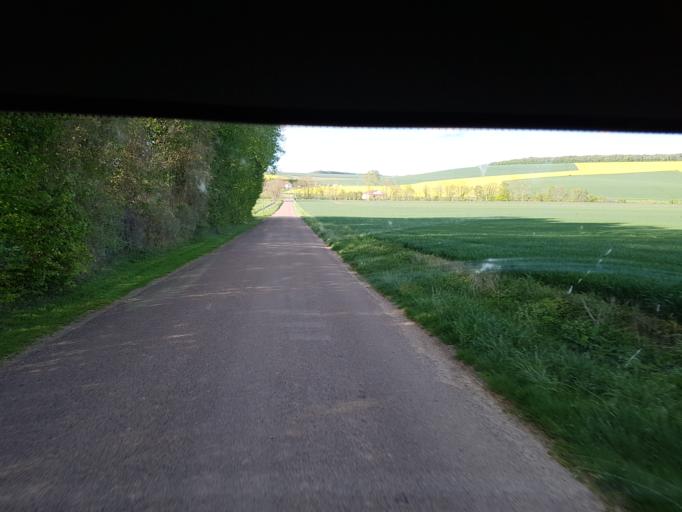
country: FR
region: Champagne-Ardenne
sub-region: Departement de l'Aube
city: Aix-en-Othe
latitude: 48.1972
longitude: 3.6347
